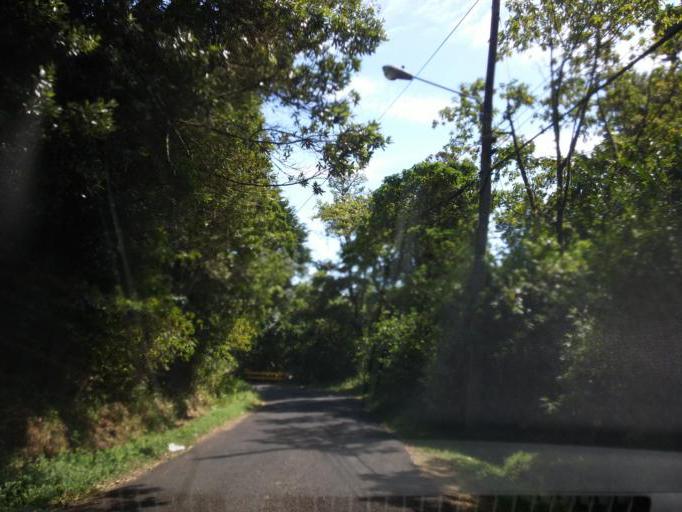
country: CR
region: Heredia
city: Santo Domingo
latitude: 10.1066
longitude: -84.1208
